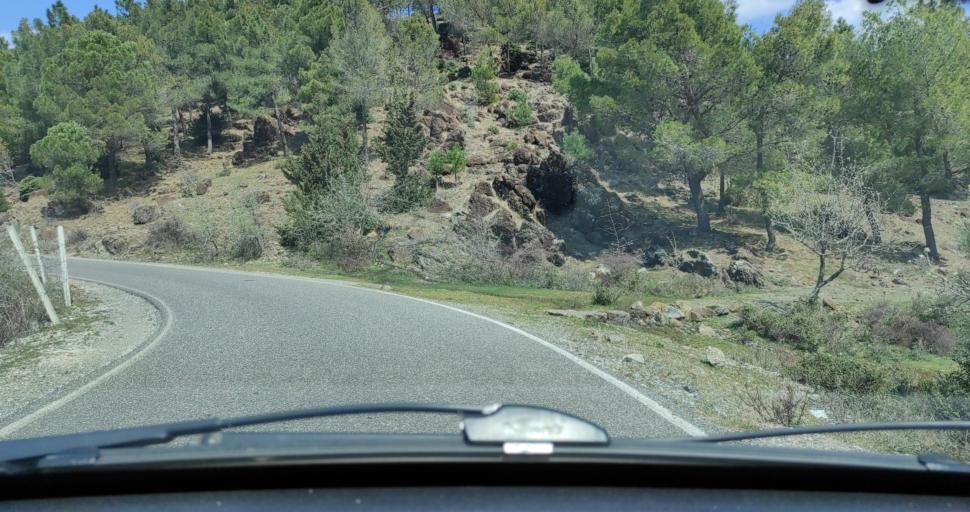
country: AL
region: Shkoder
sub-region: Rrethi i Shkodres
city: Vau i Dejes
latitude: 41.9949
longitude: 19.6495
